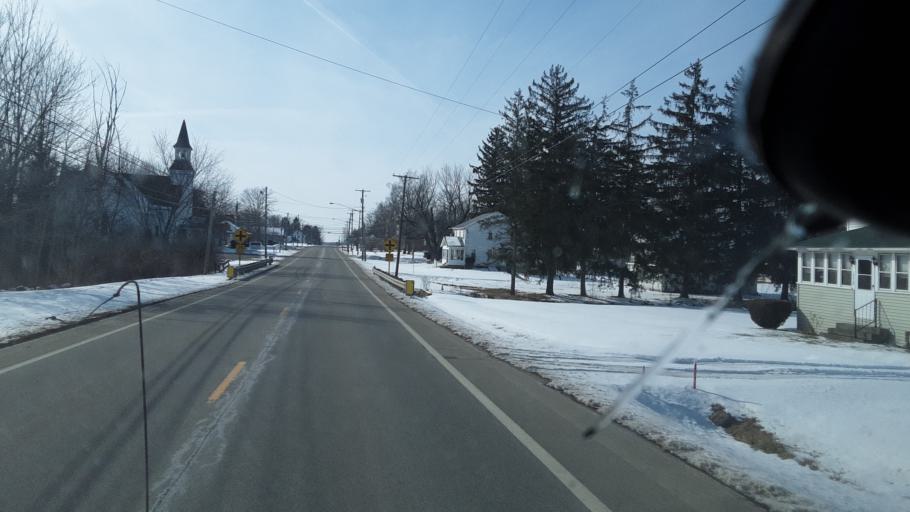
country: US
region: Ohio
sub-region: Mahoning County
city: Craig Beach
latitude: 41.0245
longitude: -80.9437
